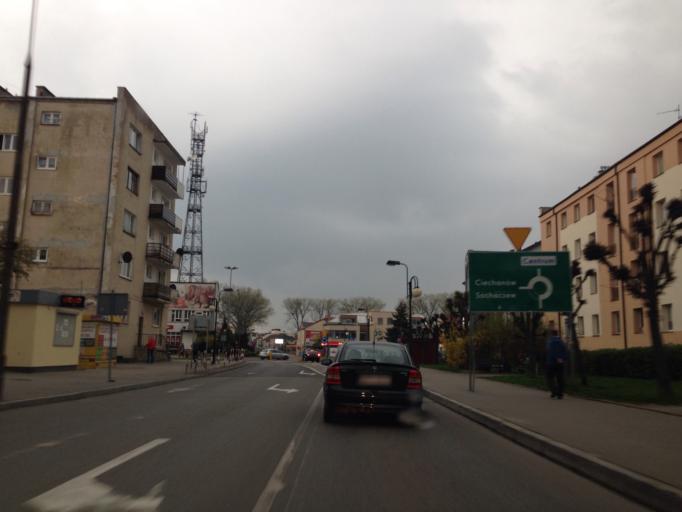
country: PL
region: Masovian Voivodeship
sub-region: Powiat plonski
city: Plonsk
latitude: 52.6296
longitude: 20.3735
